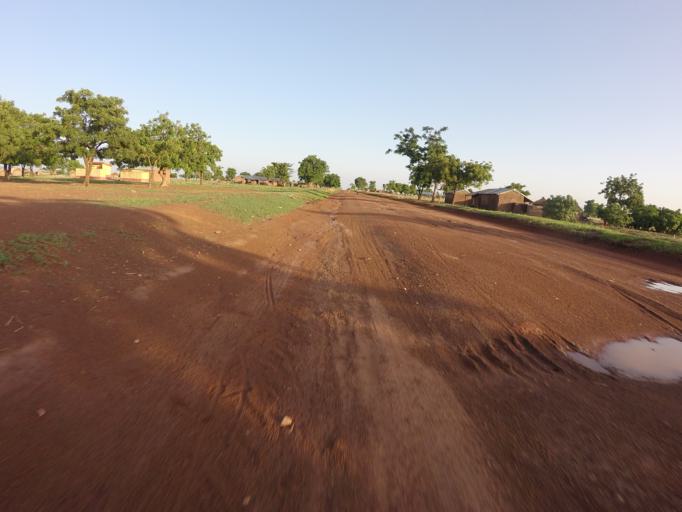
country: TG
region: Savanes
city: Sansanne-Mango
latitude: 10.2660
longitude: -0.0807
